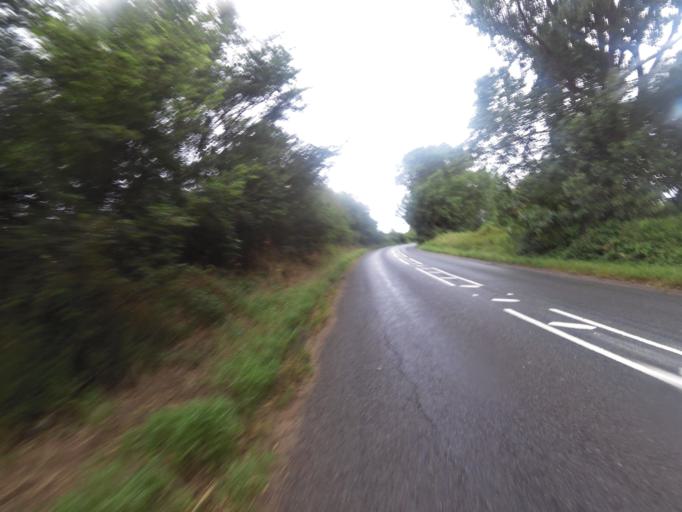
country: GB
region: England
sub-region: Suffolk
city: Bramford
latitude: 52.0931
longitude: 1.0912
